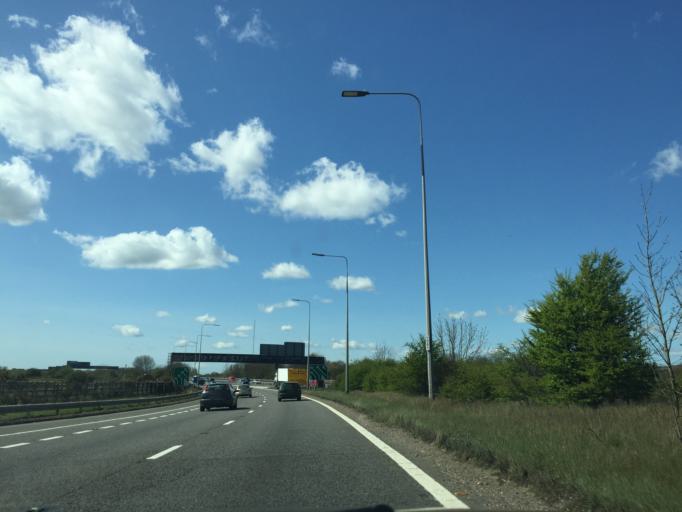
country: GB
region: England
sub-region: Hampshire
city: Havant
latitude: 50.8436
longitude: -1.0186
